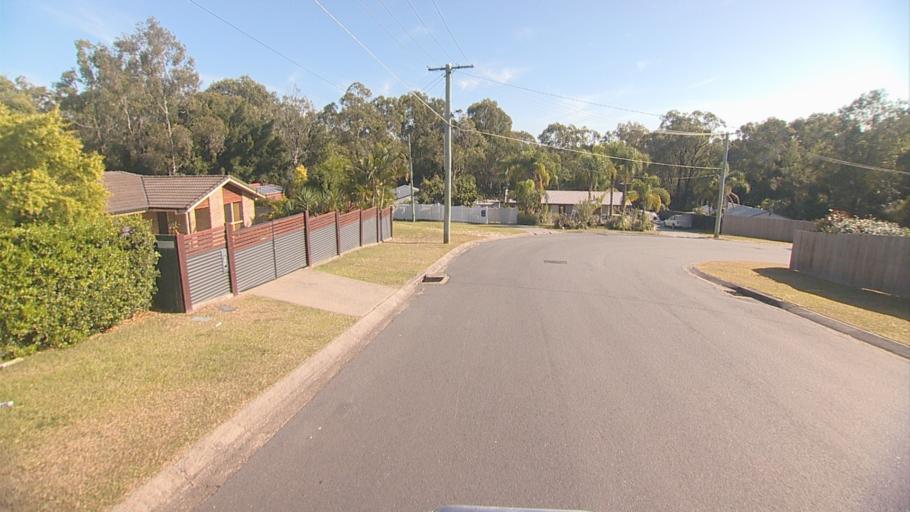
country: AU
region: Queensland
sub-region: Logan
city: Windaroo
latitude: -27.7225
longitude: 153.1836
